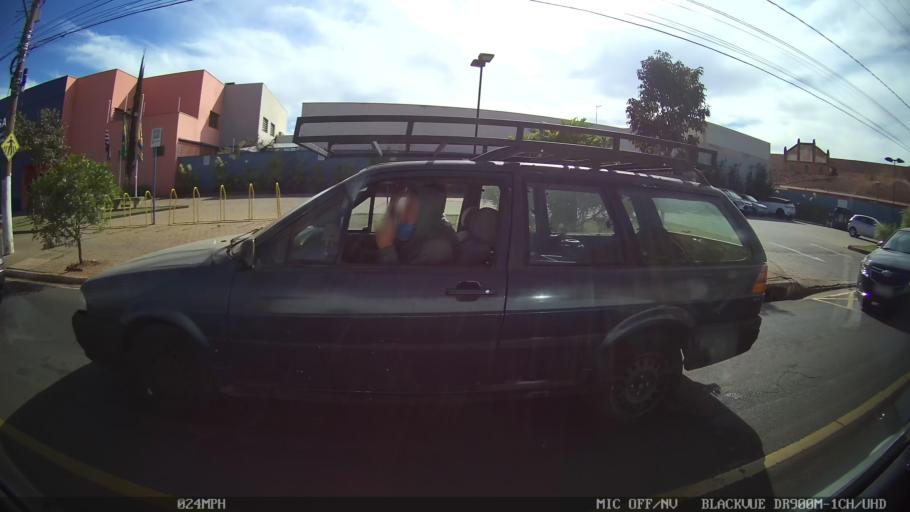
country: BR
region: Sao Paulo
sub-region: Catanduva
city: Catanduva
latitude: -21.1289
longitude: -48.9788
